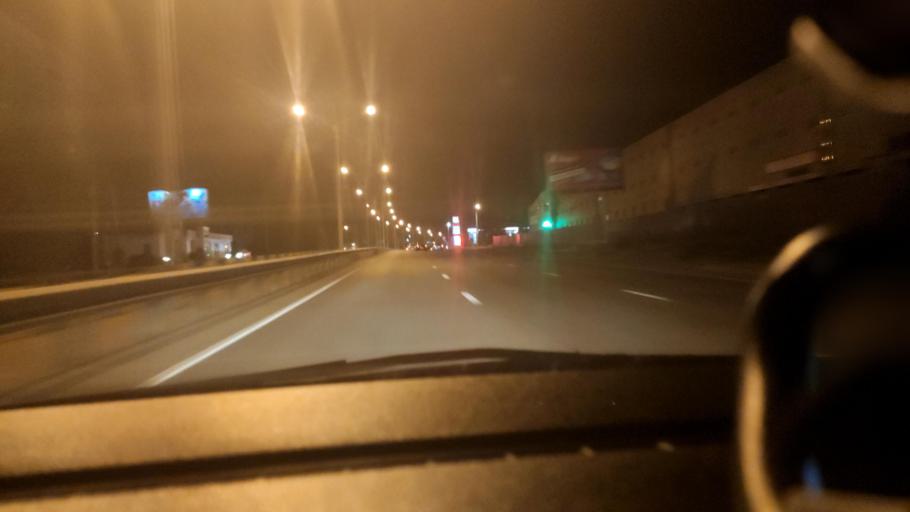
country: RU
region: Voronezj
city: Voronezh
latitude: 51.6582
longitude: 39.1336
